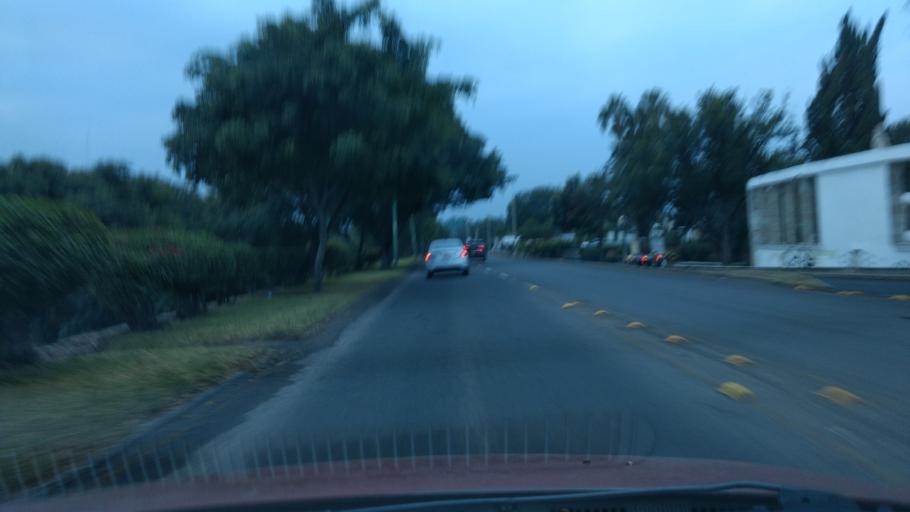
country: MX
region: Guanajuato
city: Leon
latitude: 21.1144
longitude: -101.6658
